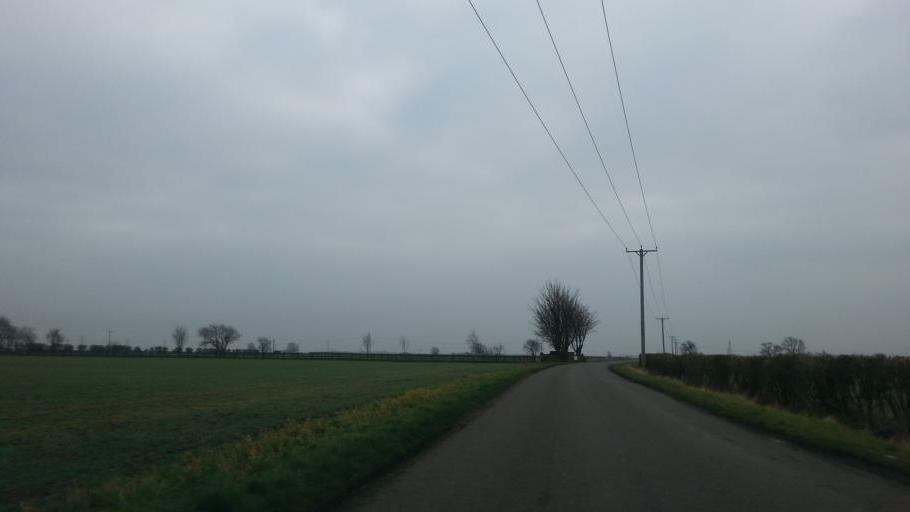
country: GB
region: England
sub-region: Lincolnshire
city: Long Bennington
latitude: 53.0050
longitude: -0.7928
